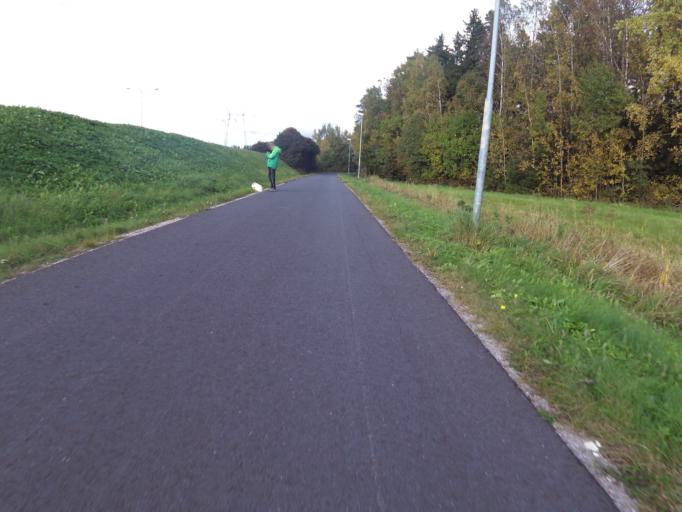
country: FI
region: Uusimaa
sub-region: Helsinki
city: Kauniainen
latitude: 60.2493
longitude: 24.7116
